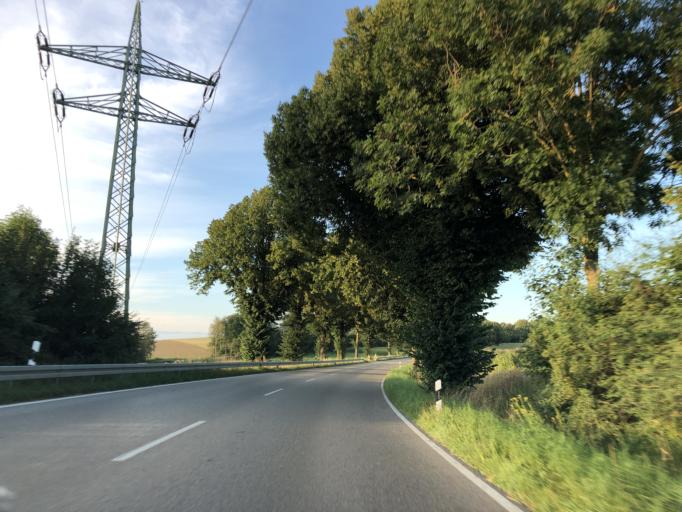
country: DE
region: Bavaria
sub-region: Upper Bavaria
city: Moosinning
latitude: 48.2549
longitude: 11.8504
